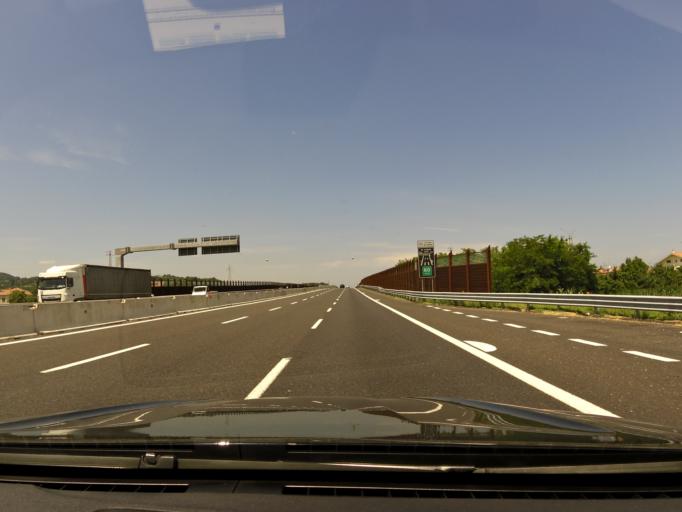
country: IT
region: The Marches
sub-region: Provincia di Pesaro e Urbino
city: Rosciano
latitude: 43.8192
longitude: 13.0045
